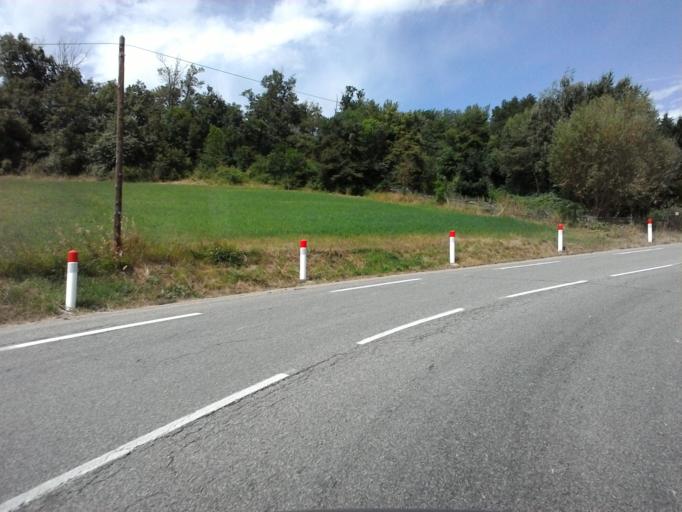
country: FR
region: Provence-Alpes-Cote d'Azur
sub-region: Departement des Hautes-Alpes
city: Gap
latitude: 44.5896
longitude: 6.0803
